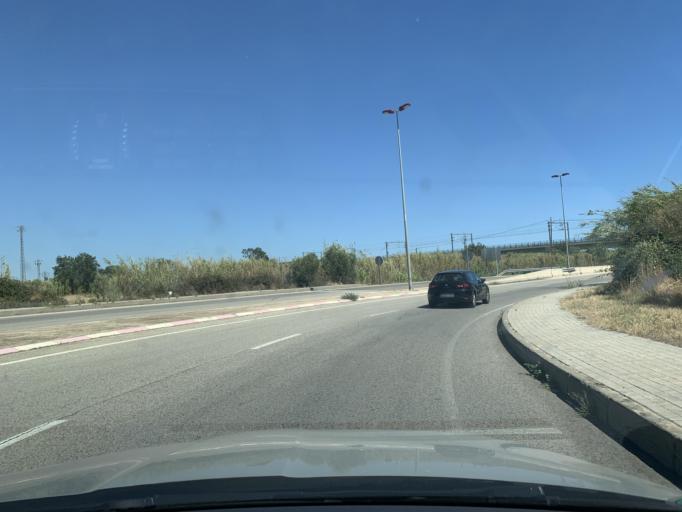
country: ES
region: Catalonia
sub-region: Provincia de Tarragona
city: Vila-seca
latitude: 41.1336
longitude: 1.1434
